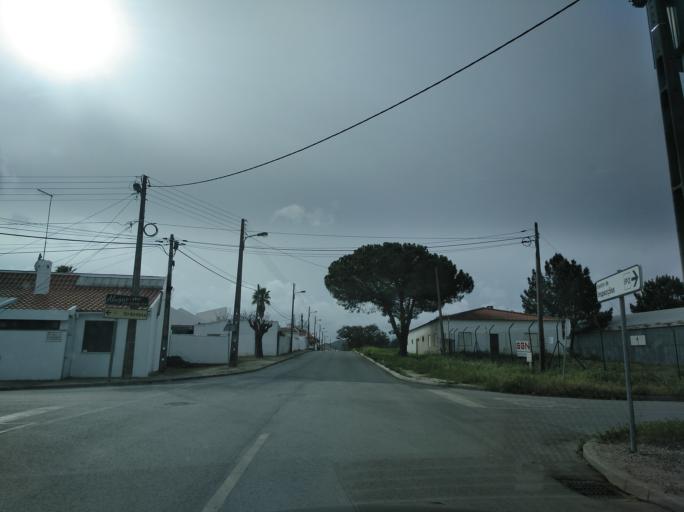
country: PT
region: Setubal
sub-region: Grandola
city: Grandola
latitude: 38.1815
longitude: -8.5567
